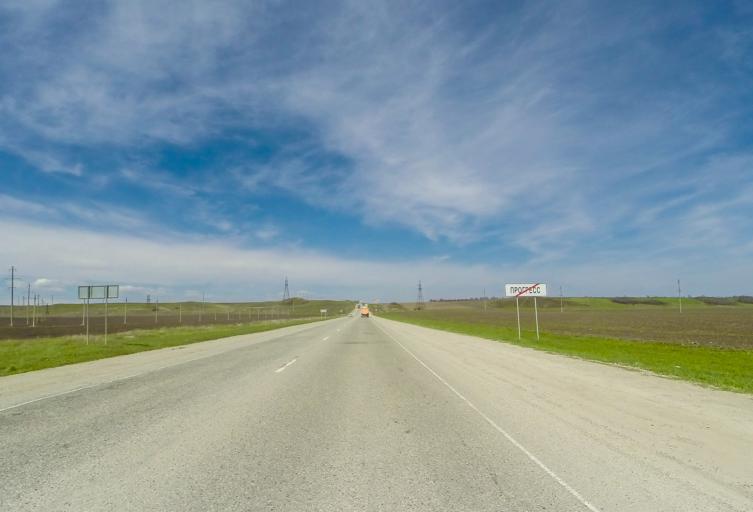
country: RU
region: Kabardino-Balkariya
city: Malka
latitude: 43.8234
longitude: 43.3263
